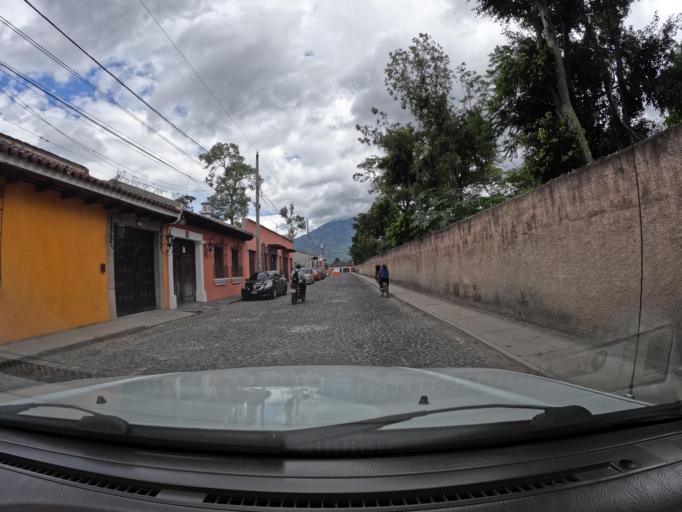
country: GT
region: Sacatepequez
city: Antigua Guatemala
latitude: 14.5616
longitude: -90.7389
